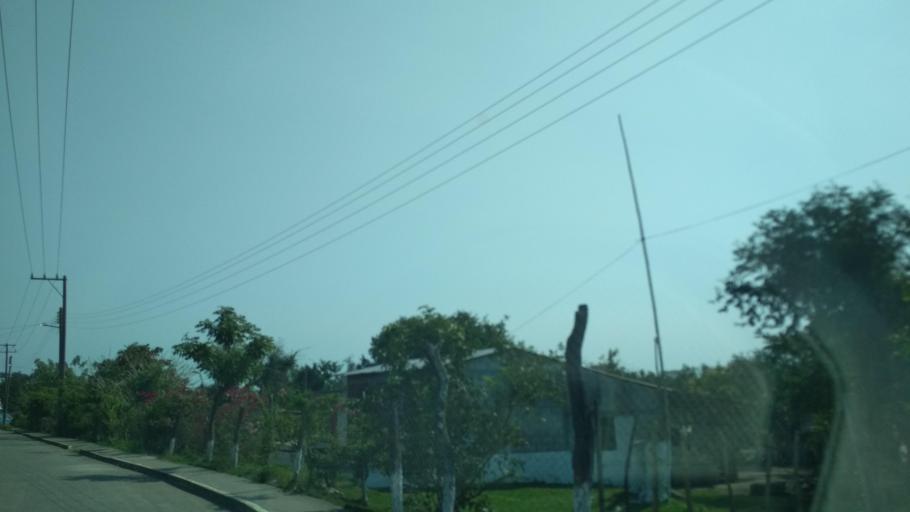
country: MX
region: Veracruz
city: Gutierrez Zamora
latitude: 20.4183
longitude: -97.1883
